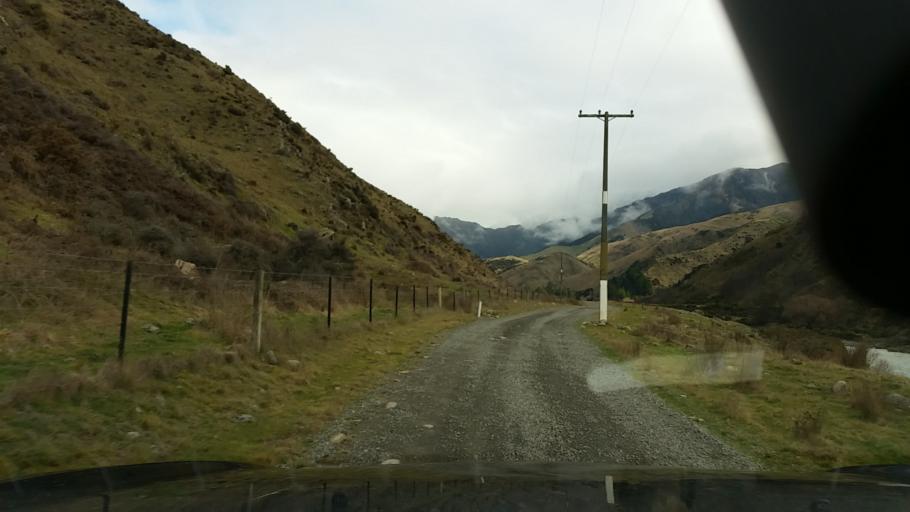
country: NZ
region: Tasman
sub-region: Tasman District
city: Richmond
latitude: -41.7312
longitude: 173.4401
